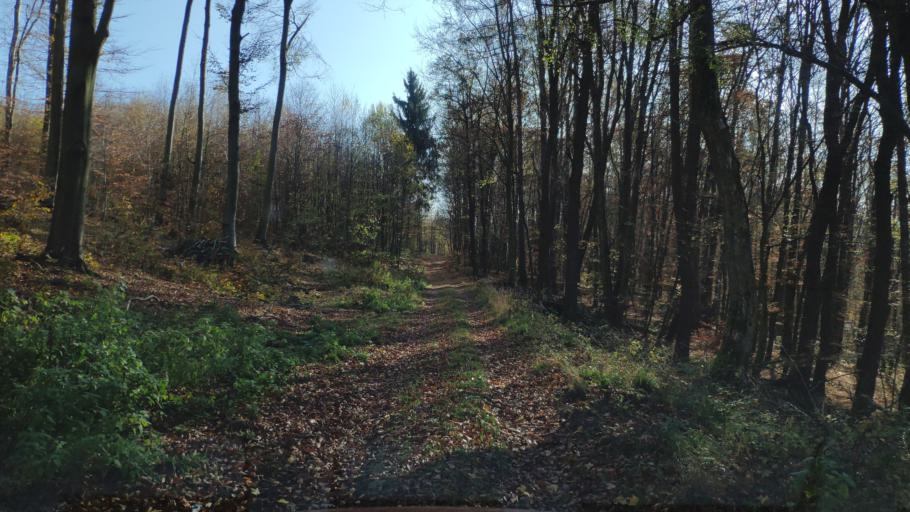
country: SK
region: Presovsky
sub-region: Okres Presov
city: Presov
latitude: 48.9019
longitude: 21.2174
